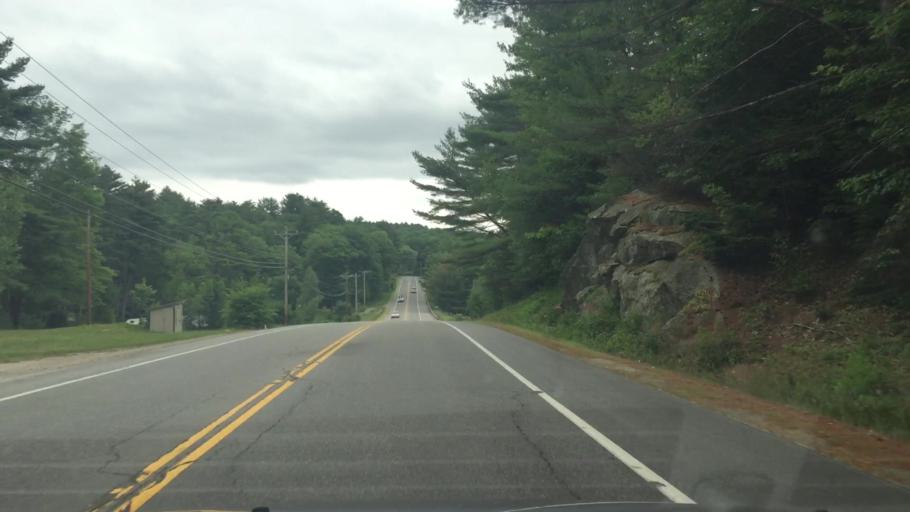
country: US
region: New Hampshire
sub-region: Belknap County
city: Meredith
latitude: 43.6219
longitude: -71.5626
